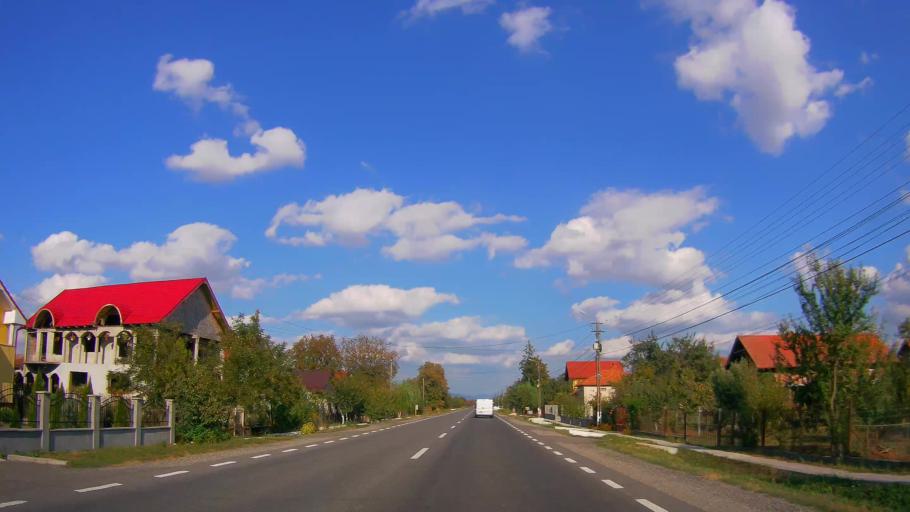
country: RO
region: Satu Mare
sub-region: Comuna Agris
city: Agris
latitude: 47.8676
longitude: 23.0056
